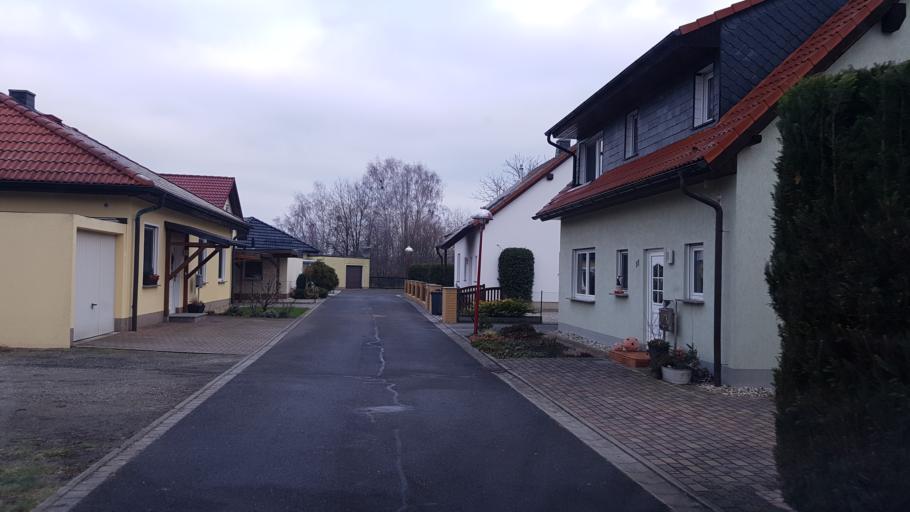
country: DE
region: Brandenburg
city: Schipkau
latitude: 51.5447
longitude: 13.8924
